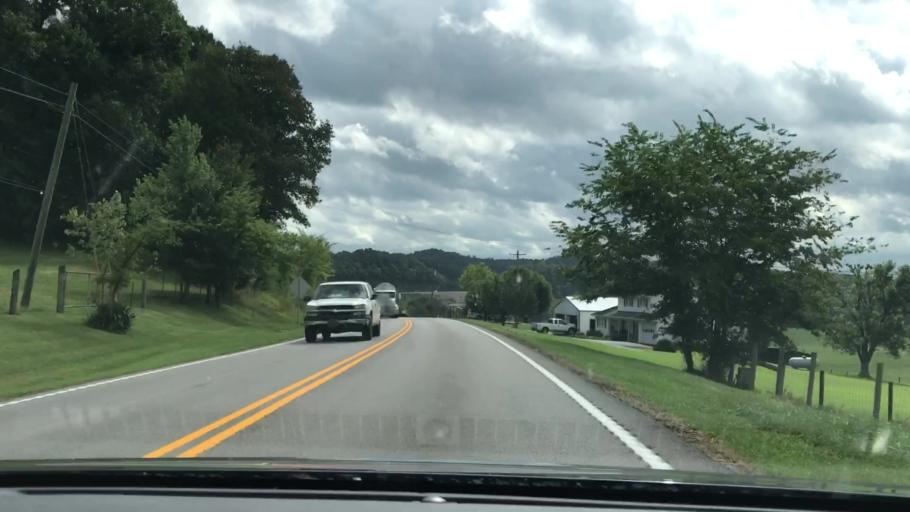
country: US
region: Kentucky
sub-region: Cumberland County
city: Burkesville
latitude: 36.8008
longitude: -85.4228
